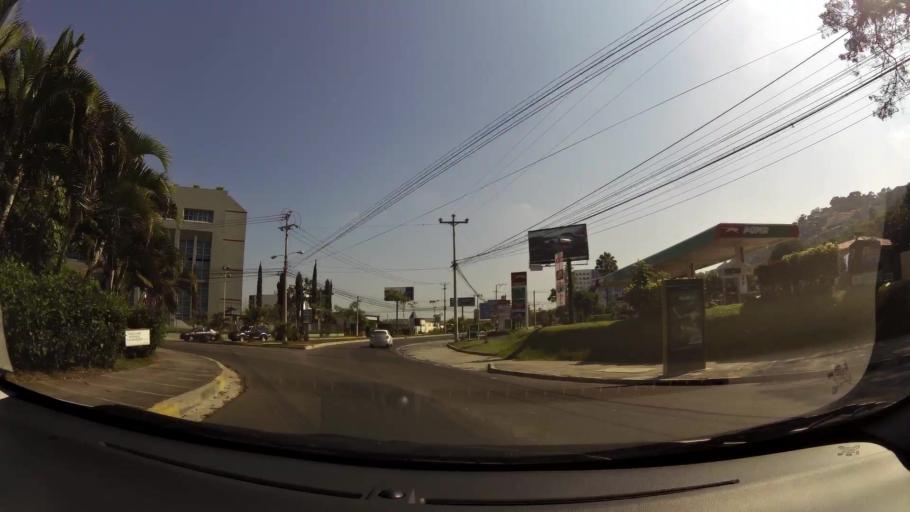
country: SV
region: La Libertad
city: Antiguo Cuscatlan
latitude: 13.6616
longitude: -89.2552
